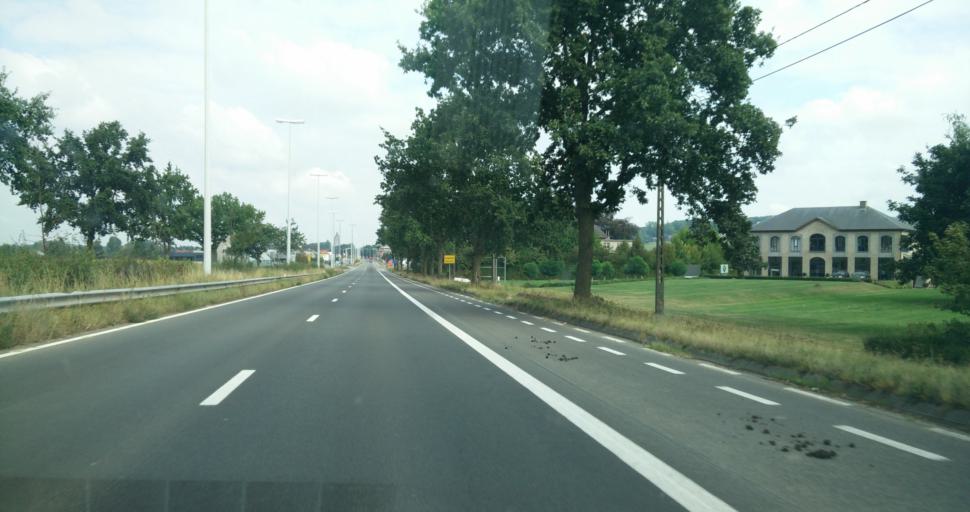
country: BE
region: Flanders
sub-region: Provincie Oost-Vlaanderen
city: Oudenaarde
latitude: 50.8206
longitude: 3.6039
